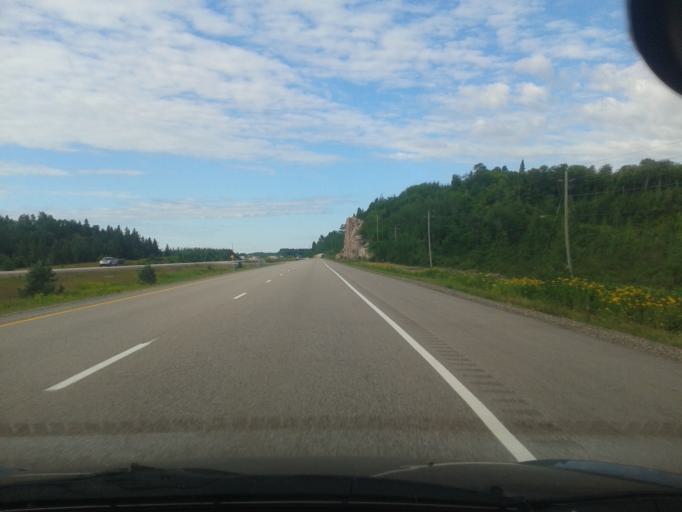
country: CA
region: Ontario
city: Powassan
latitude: 46.0189
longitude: -79.3444
